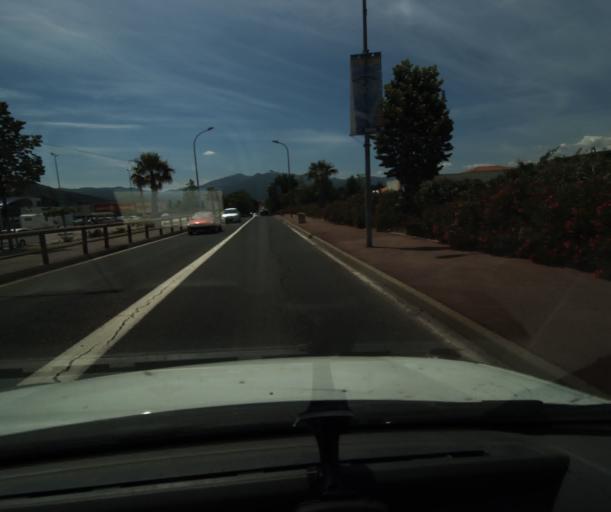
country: FR
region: Languedoc-Roussillon
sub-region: Departement des Pyrenees-Orientales
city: el Volo
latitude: 42.5314
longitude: 2.8390
